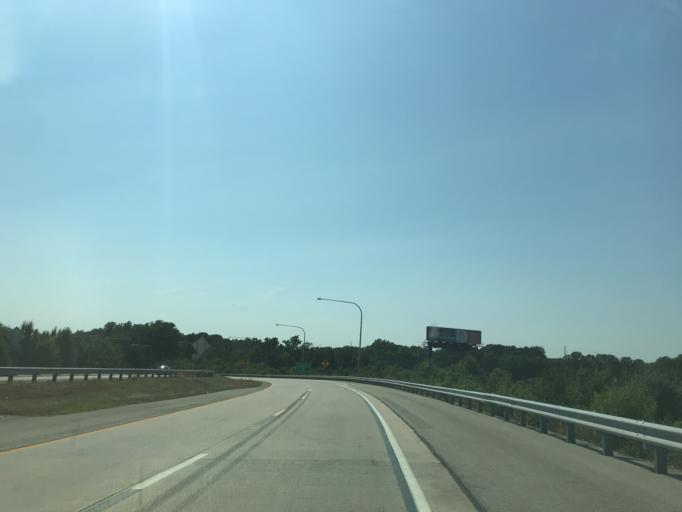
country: US
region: Delaware
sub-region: New Castle County
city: Brookside
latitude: 39.6857
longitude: -75.7036
